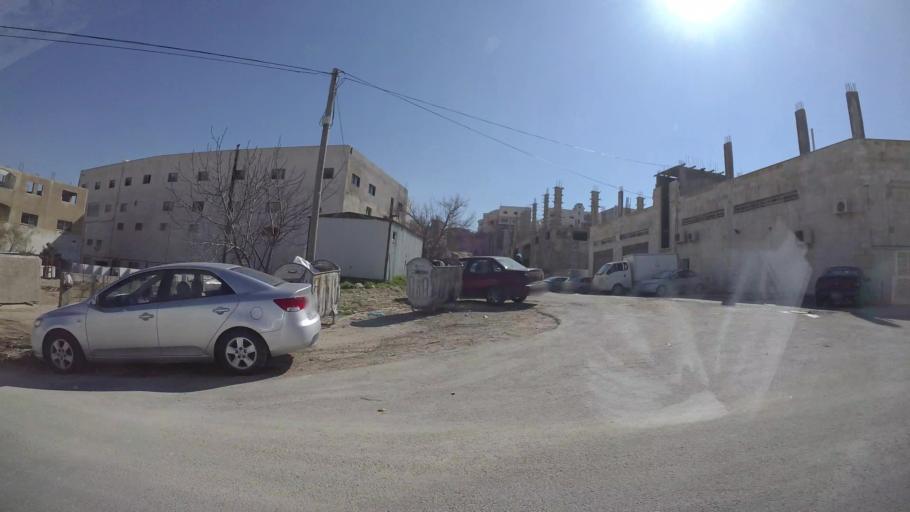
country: JO
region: Amman
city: Al Bunayyat ash Shamaliyah
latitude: 31.9140
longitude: 35.9064
